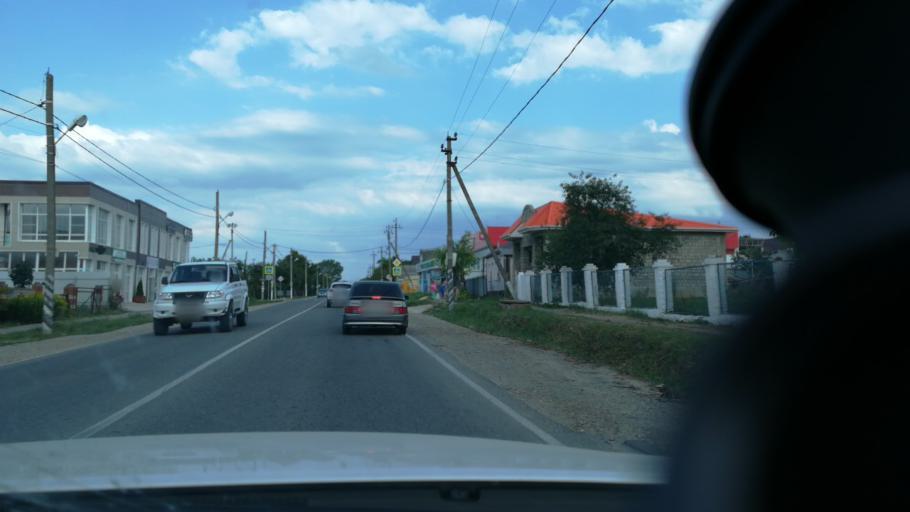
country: RU
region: Krasnodarskiy
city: Gostagayevskaya
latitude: 45.0258
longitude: 37.4965
